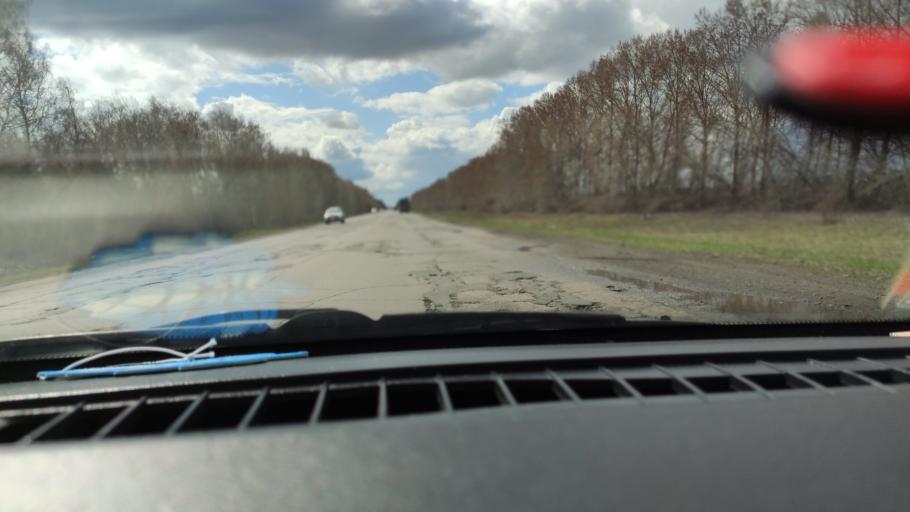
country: RU
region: Samara
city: Tol'yatti
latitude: 53.6376
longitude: 49.4193
